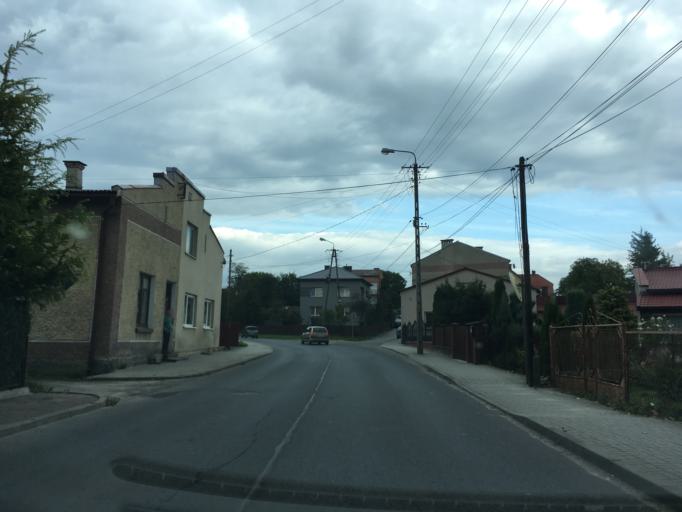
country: PL
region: Lesser Poland Voivodeship
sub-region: Powiat olkuski
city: Wolbrom
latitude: 50.3893
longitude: 19.7603
